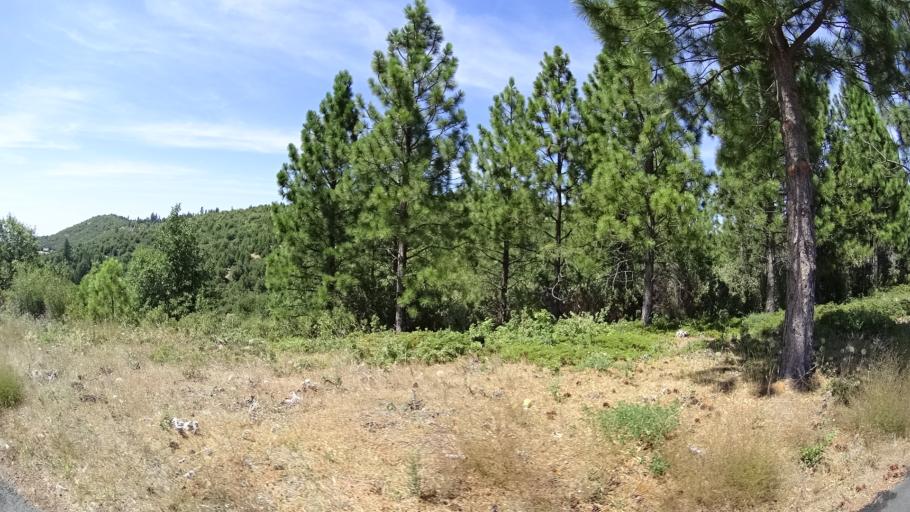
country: US
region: California
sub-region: Calaveras County
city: Forest Meadows
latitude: 38.1852
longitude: -120.4125
